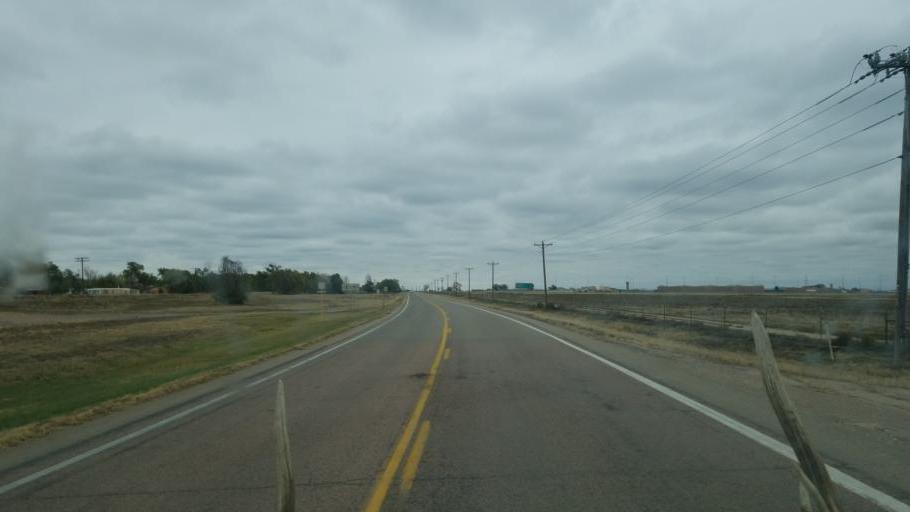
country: US
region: Colorado
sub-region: Crowley County
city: Ordway
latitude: 38.1915
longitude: -103.8572
